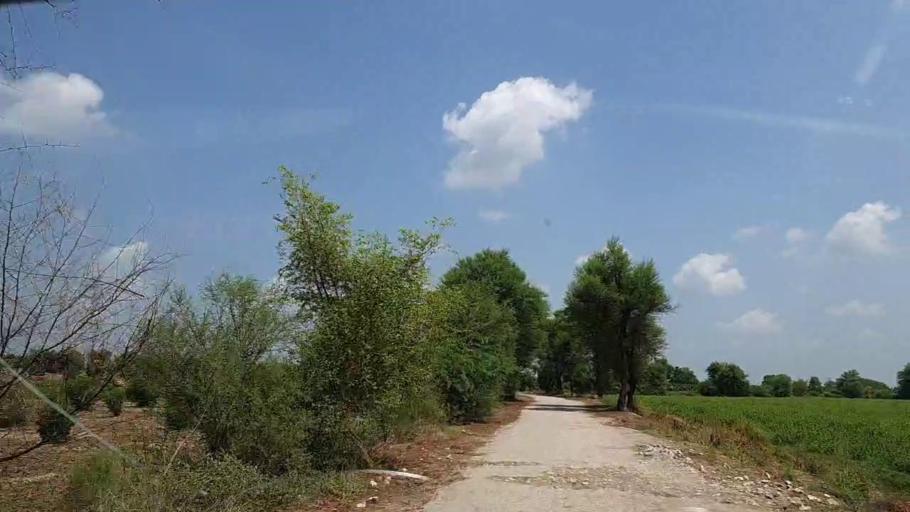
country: PK
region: Sindh
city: Tharu Shah
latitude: 27.0001
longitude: 68.0623
